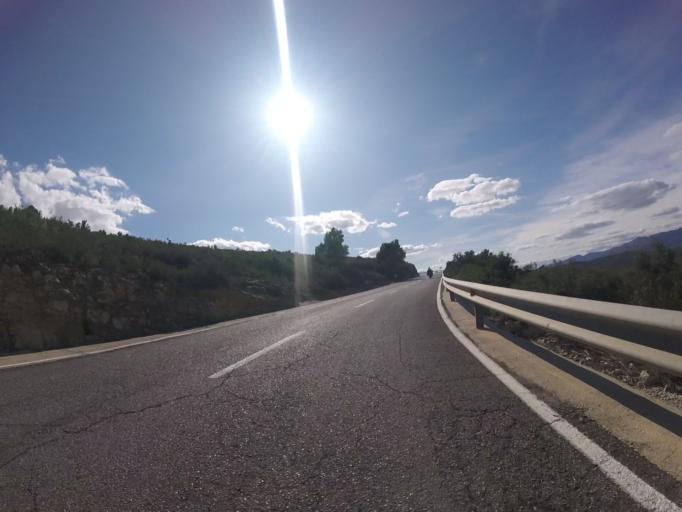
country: ES
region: Valencia
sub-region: Provincia de Castello
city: Cuevas de Vinroma
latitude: 40.2964
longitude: 0.1738
